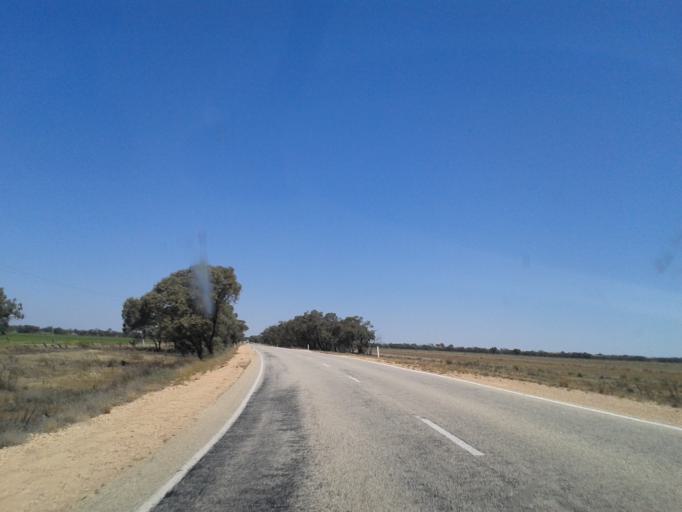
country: AU
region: Victoria
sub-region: Swan Hill
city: Swan Hill
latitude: -34.9373
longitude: 143.3001
